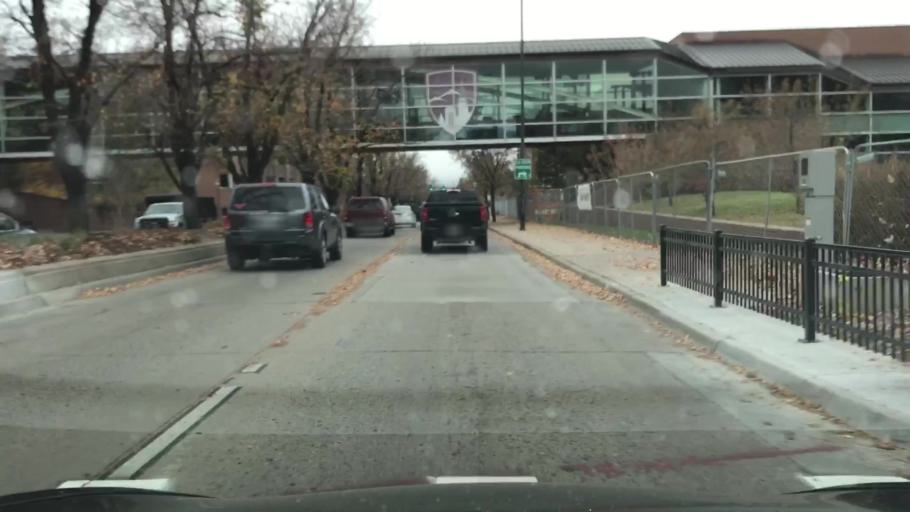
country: US
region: Colorado
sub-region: Arapahoe County
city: Cherry Hills Village
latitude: 39.6785
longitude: -104.9624
